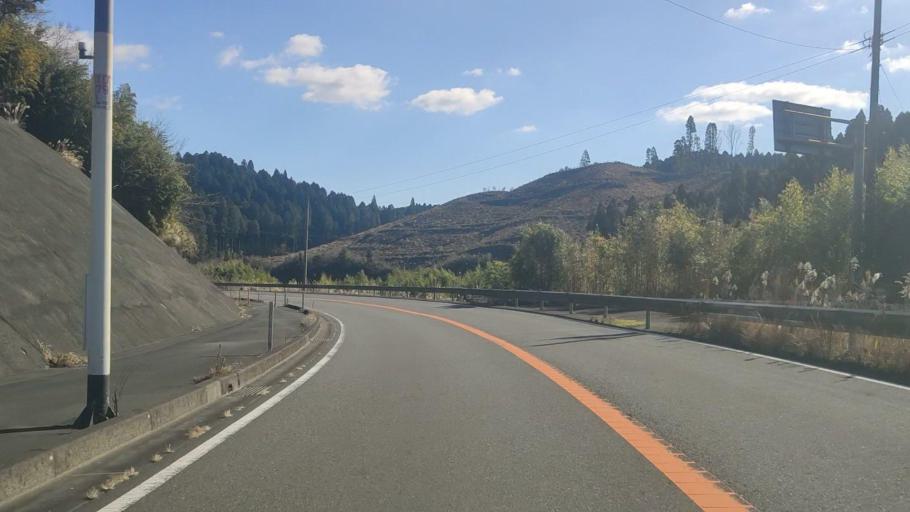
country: JP
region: Kagoshima
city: Sueyoshicho-ninokata
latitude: 31.6611
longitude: 130.8951
